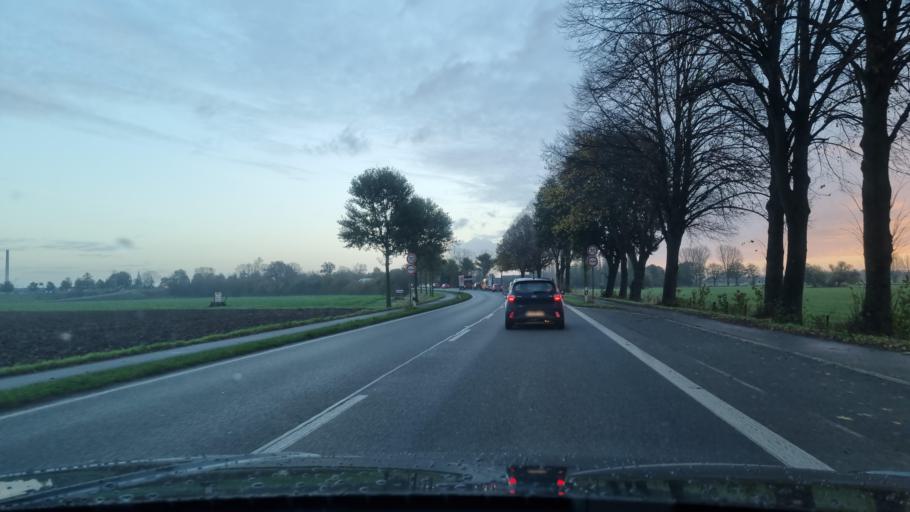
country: DE
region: North Rhine-Westphalia
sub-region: Regierungsbezirk Dusseldorf
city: Emmerich
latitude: 51.8177
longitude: 6.2215
